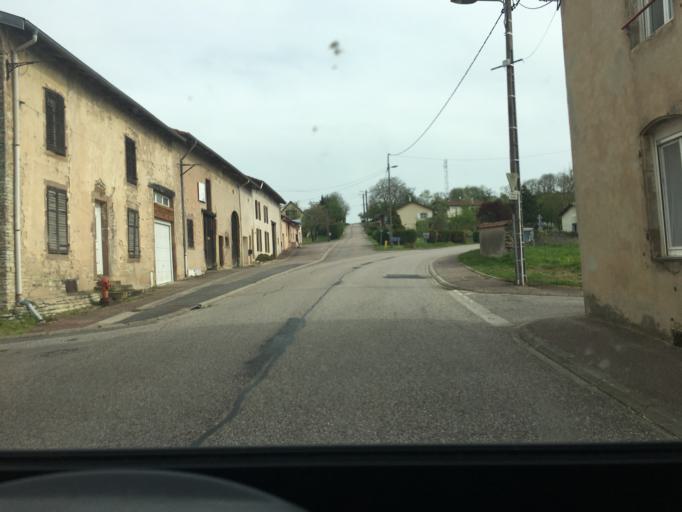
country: FR
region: Lorraine
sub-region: Departement de Meurthe-et-Moselle
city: Einville-au-Jard
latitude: 48.6798
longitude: 6.4917
